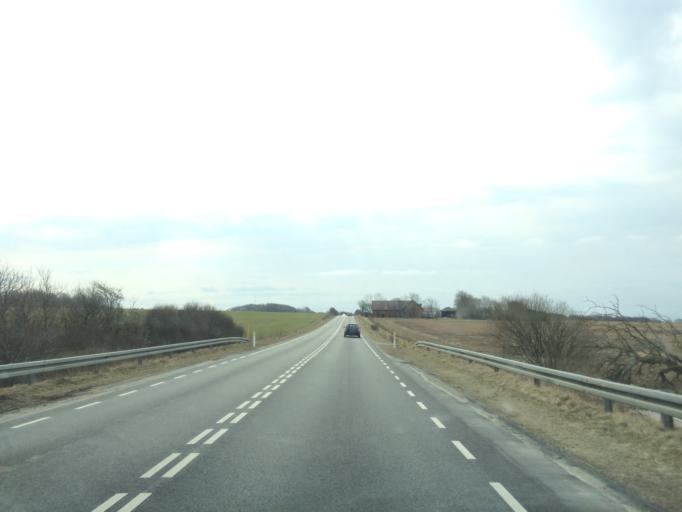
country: DK
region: Central Jutland
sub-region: Ringkobing-Skjern Kommune
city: Skjern
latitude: 55.9989
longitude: 8.5041
